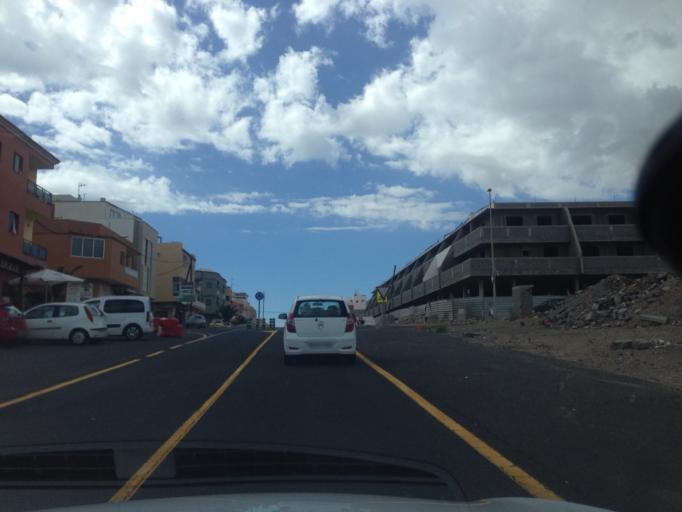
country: ES
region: Canary Islands
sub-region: Provincia de Santa Cruz de Tenerife
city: San Isidro
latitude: 28.0302
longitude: -16.5893
